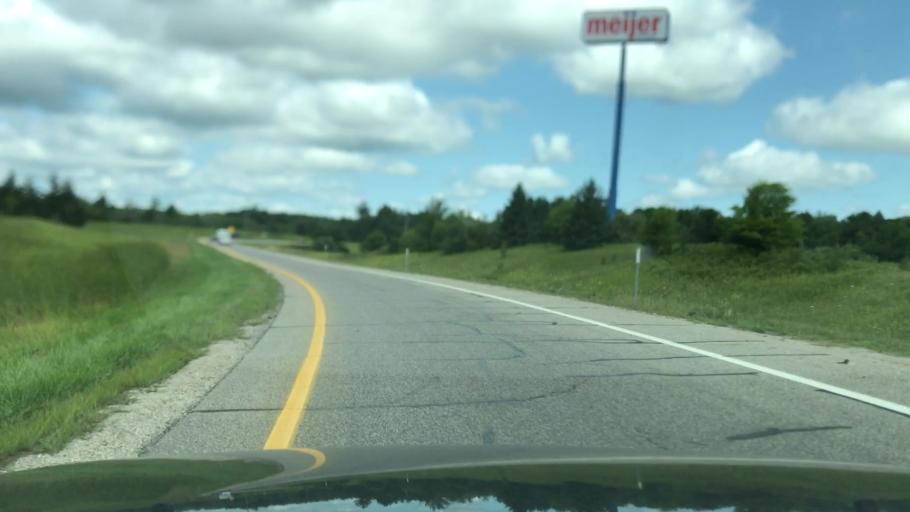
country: US
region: Michigan
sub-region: Mecosta County
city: Big Rapids
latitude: 43.6890
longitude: -85.5190
